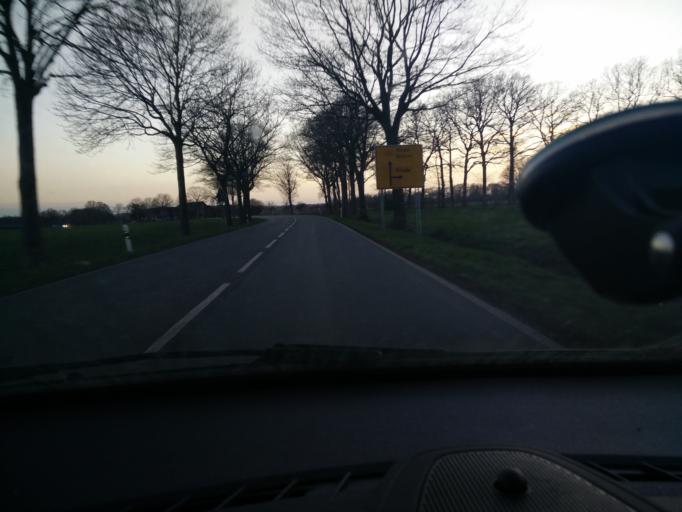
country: DE
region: North Rhine-Westphalia
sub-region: Regierungsbezirk Munster
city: Rhede
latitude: 51.7436
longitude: 6.7329
